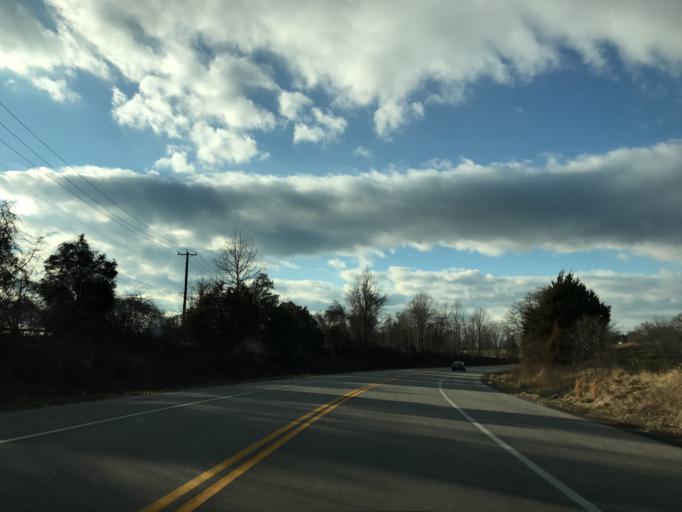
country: US
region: Maryland
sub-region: Cecil County
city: Rising Sun
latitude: 39.6625
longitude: -76.0118
